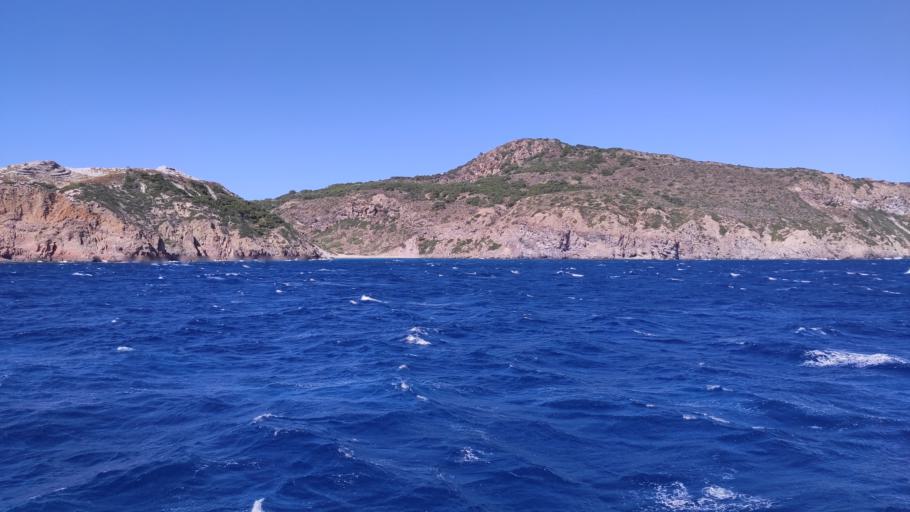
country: GR
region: South Aegean
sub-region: Nomos Dodekanisou
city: Mandraki
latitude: 36.6744
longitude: 27.1474
